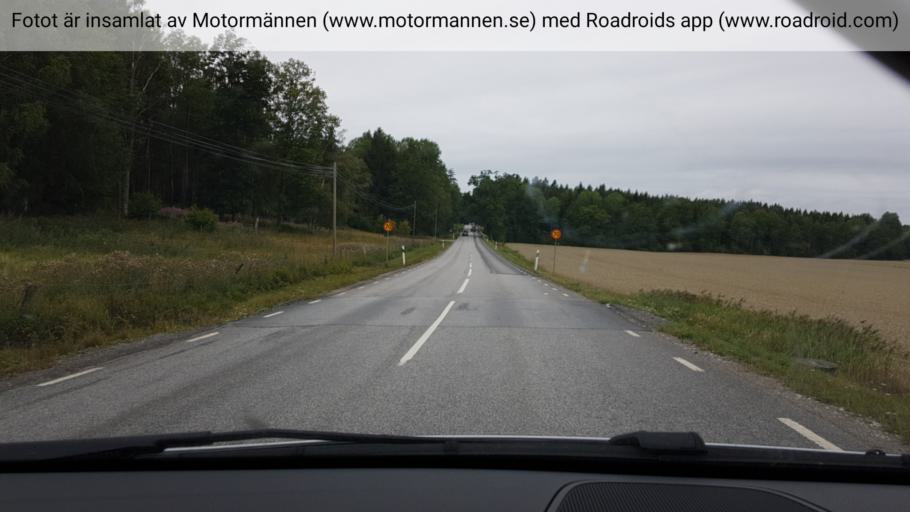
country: SE
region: Stockholm
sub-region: Nykvarns Kommun
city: Nykvarn
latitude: 59.2053
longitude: 17.3981
